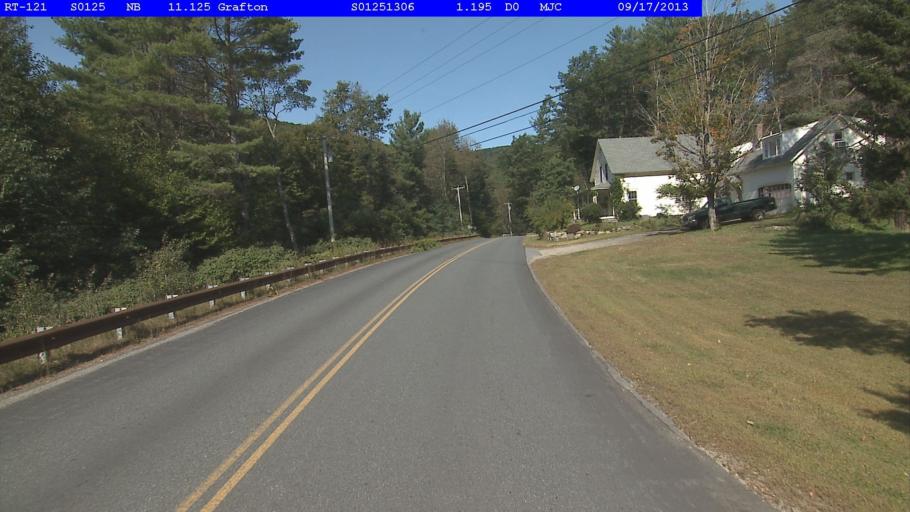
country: US
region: Vermont
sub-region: Windham County
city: Rockingham
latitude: 43.1571
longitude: -72.5752
